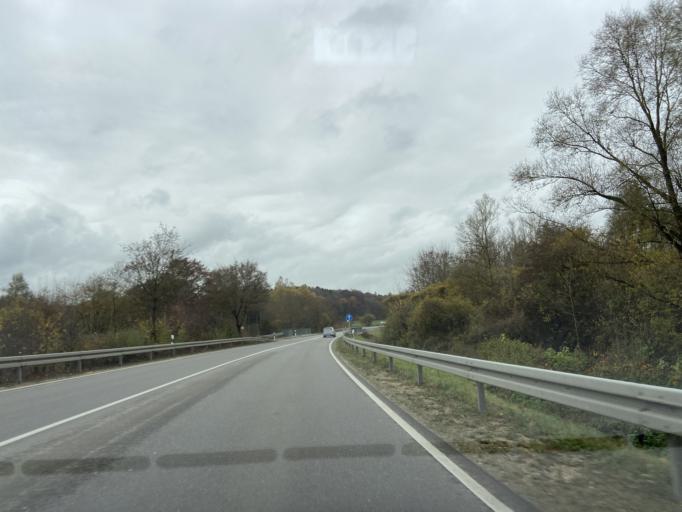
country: DE
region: Baden-Wuerttemberg
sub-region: Tuebingen Region
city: Krauchenwies
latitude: 48.0308
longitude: 9.2487
